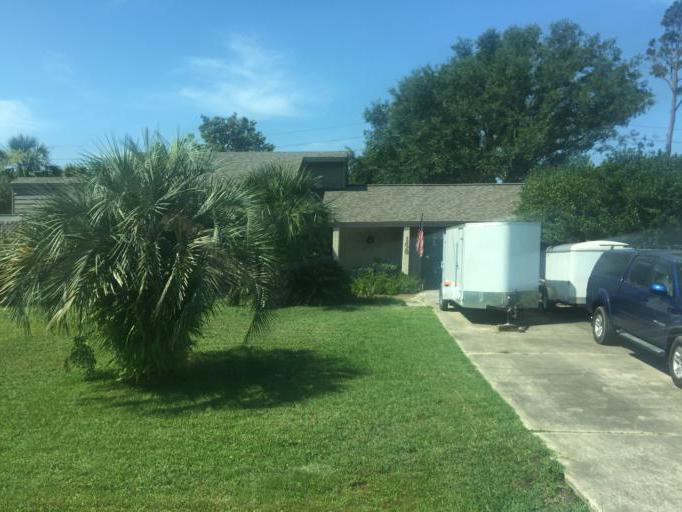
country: US
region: Florida
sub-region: Bay County
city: Panama City Beach
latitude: 30.1700
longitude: -85.7844
